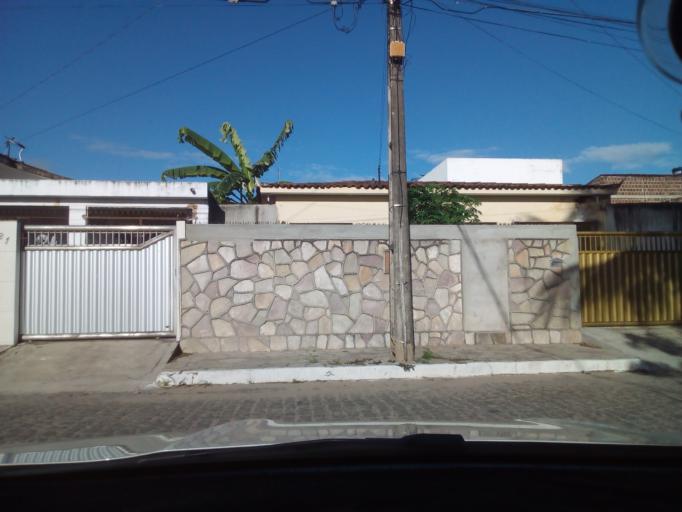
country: BR
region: Paraiba
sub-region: Joao Pessoa
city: Joao Pessoa
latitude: -7.1834
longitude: -34.8375
